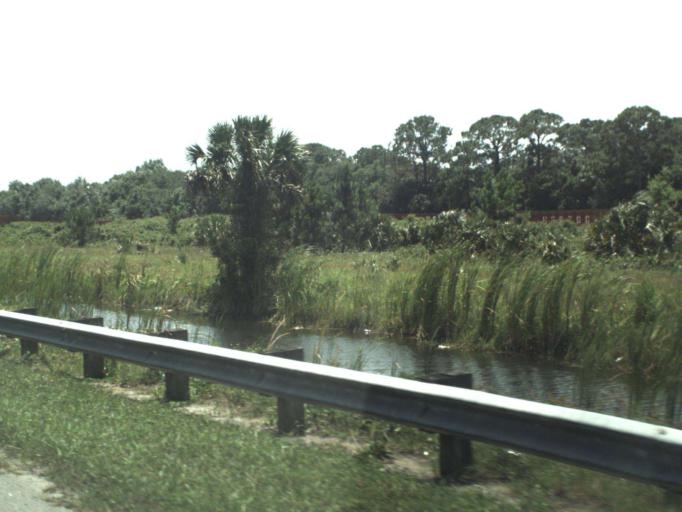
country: US
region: Florida
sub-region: Volusia County
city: New Smyrna Beach
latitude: 29.0095
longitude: -80.9201
